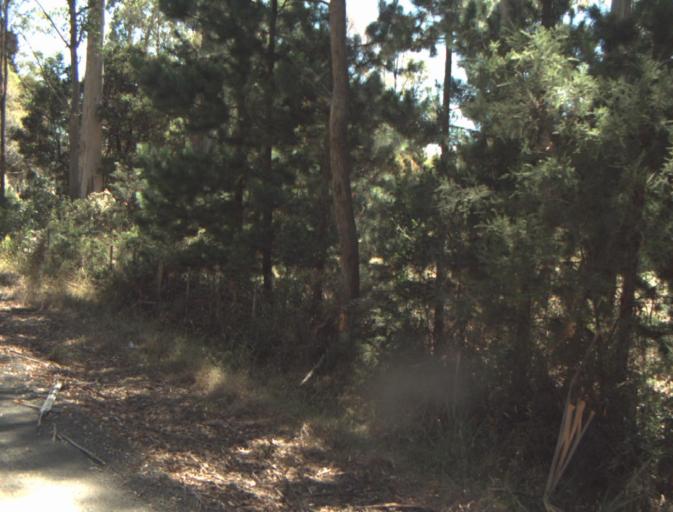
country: AU
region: Tasmania
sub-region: Launceston
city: Newstead
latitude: -41.3428
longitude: 147.3679
